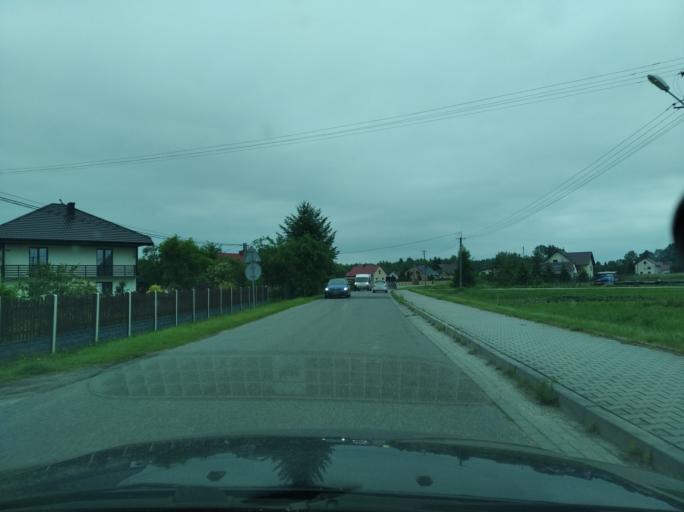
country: PL
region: Subcarpathian Voivodeship
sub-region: Powiat kolbuszowski
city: Niwiska
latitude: 50.1558
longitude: 21.6693
